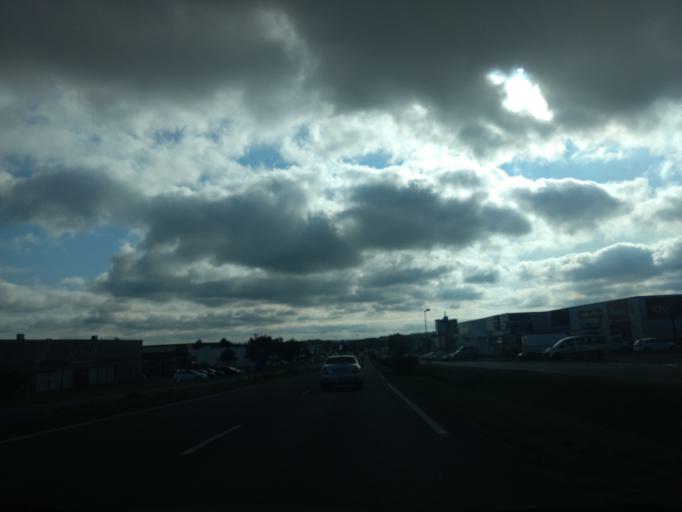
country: FR
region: Poitou-Charentes
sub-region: Departement de la Vienne
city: Chasseneuil-du-Poitou
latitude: 46.6518
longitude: 0.3644
